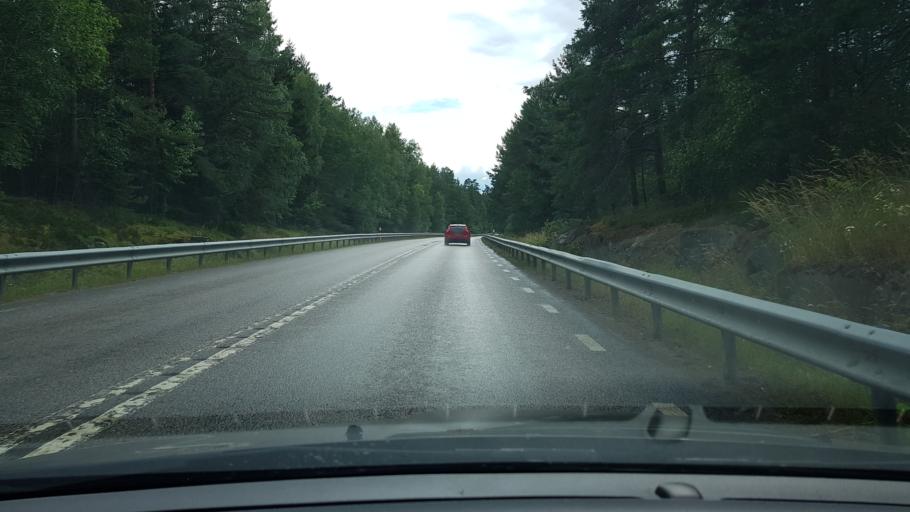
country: SE
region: Uppsala
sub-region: Uppsala Kommun
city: Saevja
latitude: 59.7969
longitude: 17.6803
